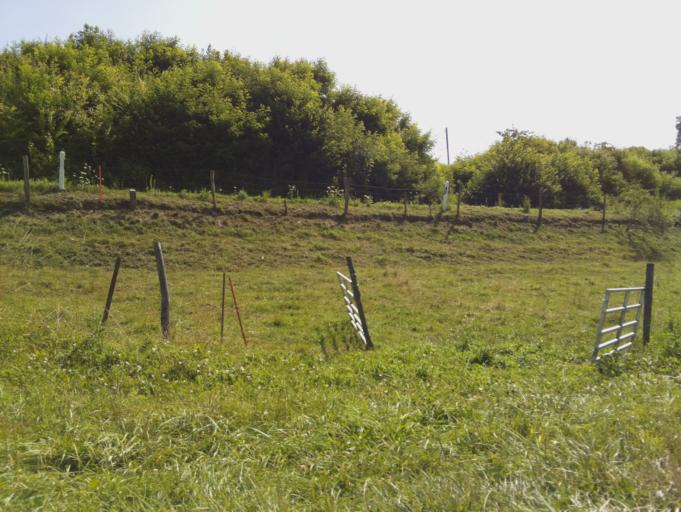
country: CH
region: Zurich
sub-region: Bezirk Andelfingen
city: Grossandelfingen
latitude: 47.5878
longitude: 8.6678
